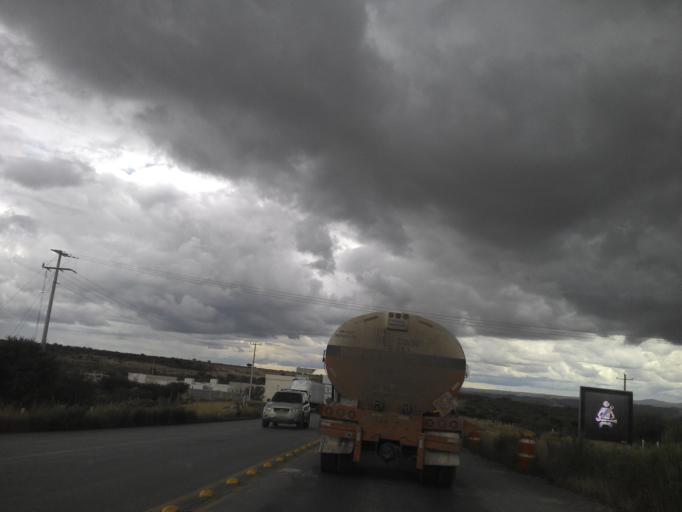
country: MX
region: Zacatecas
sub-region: Rio Grande
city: Los Condes
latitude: 23.8725
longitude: -103.0865
